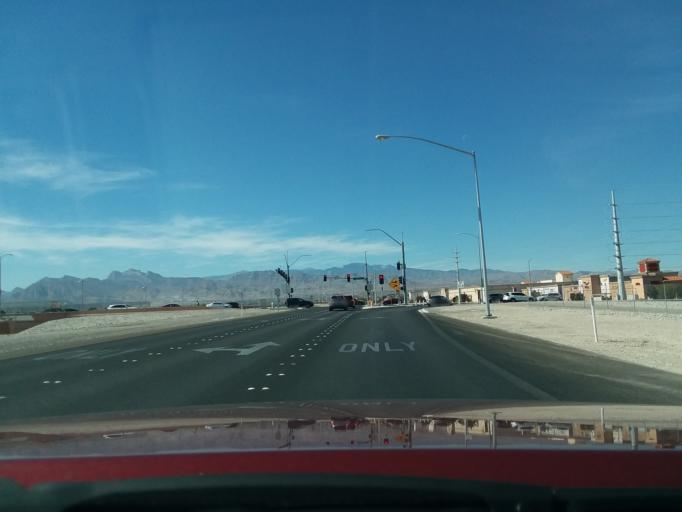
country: US
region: Nevada
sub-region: Clark County
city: North Las Vegas
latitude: 36.2758
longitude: -115.2053
